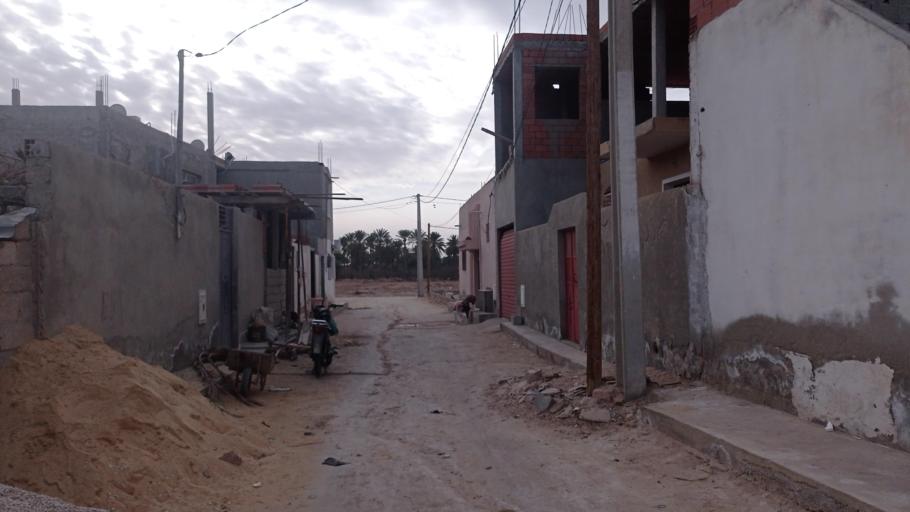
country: TN
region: Qabis
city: Gabes
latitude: 33.8356
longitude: 10.1157
